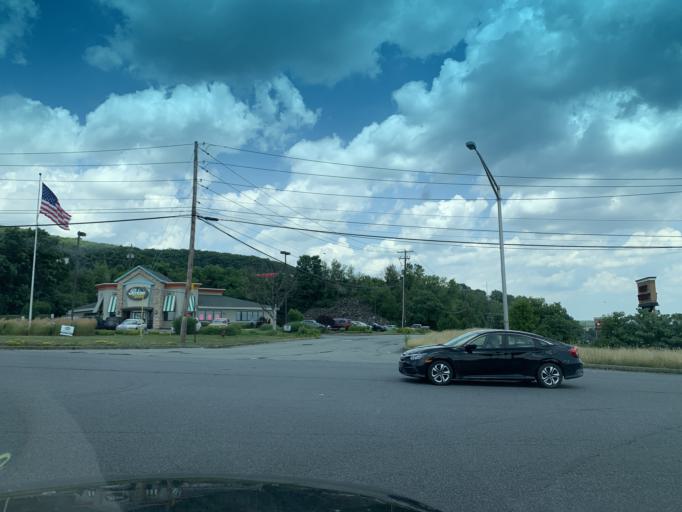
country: US
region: Pennsylvania
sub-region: Lackawanna County
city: Chinchilla
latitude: 41.4620
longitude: -75.6518
